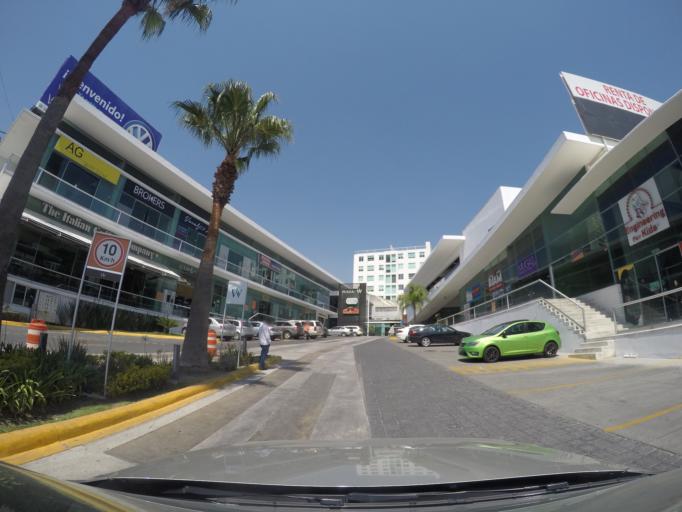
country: MX
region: Puebla
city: Tlazcalancingo
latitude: 19.0174
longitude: -98.2519
